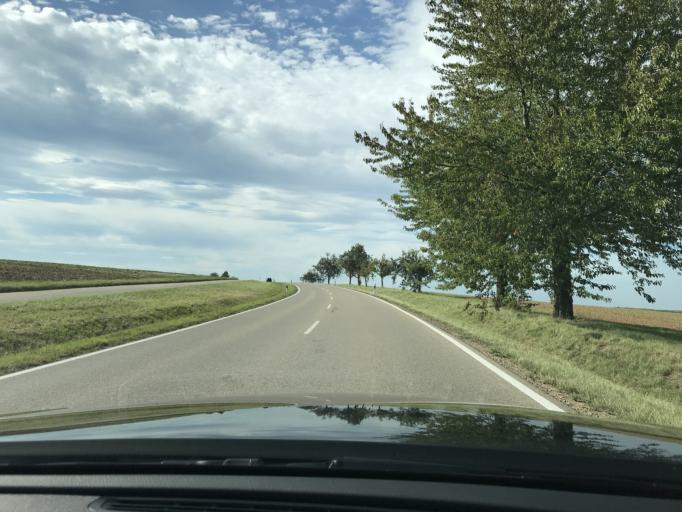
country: DE
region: Baden-Wuerttemberg
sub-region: Regierungsbezirk Stuttgart
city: Schwaikheim
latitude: 48.8966
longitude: 9.3615
